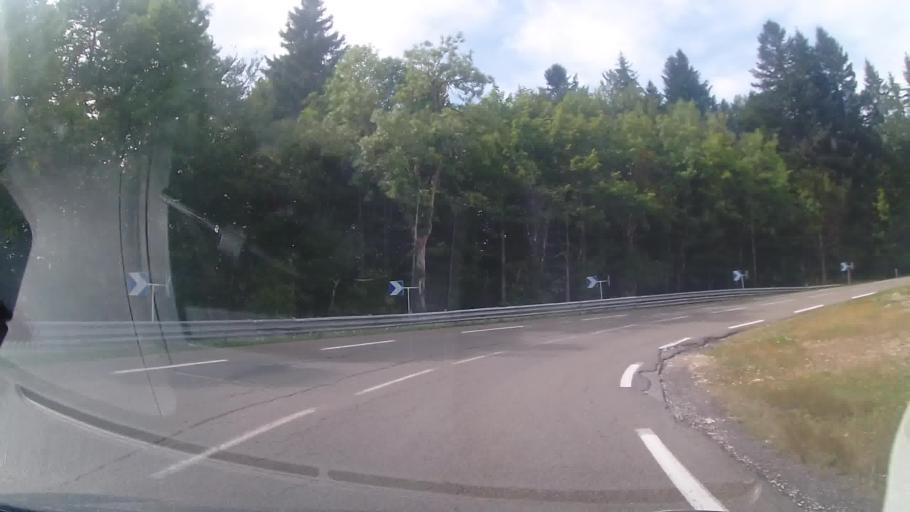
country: FR
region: Franche-Comte
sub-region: Departement du Jura
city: Les Rousses
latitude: 46.4138
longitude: 6.0598
